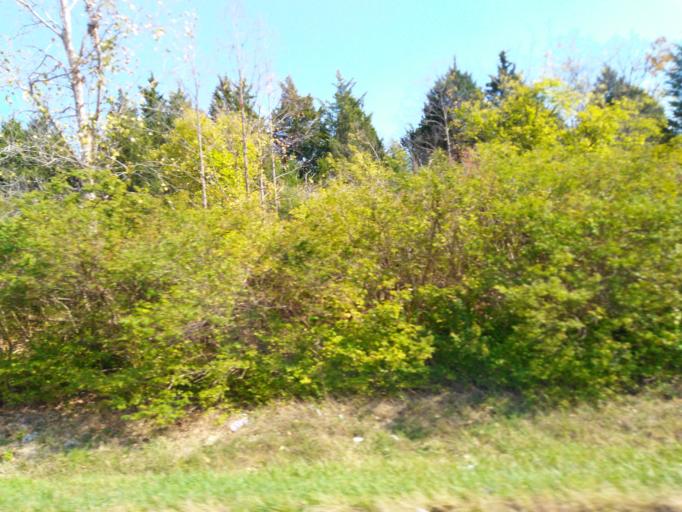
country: US
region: Missouri
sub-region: Saint Louis County
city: Sunset Hills
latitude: 38.5396
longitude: -90.4170
